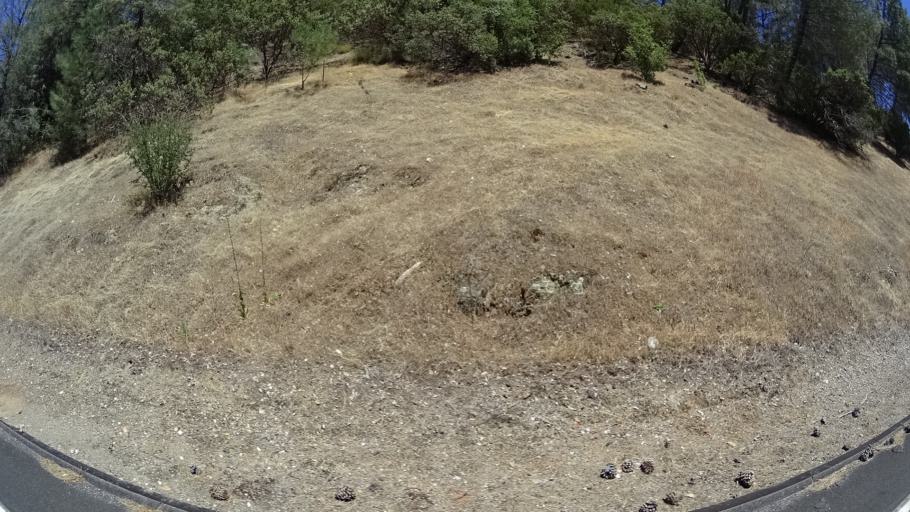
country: US
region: California
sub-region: Calaveras County
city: San Andreas
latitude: 38.2629
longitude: -120.7145
